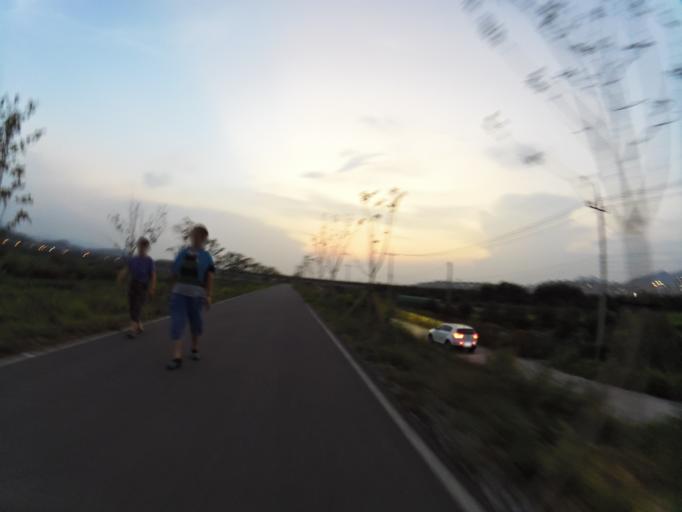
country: KR
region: Gyeongsangbuk-do
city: Gyeongsan-si
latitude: 35.8587
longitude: 128.7309
